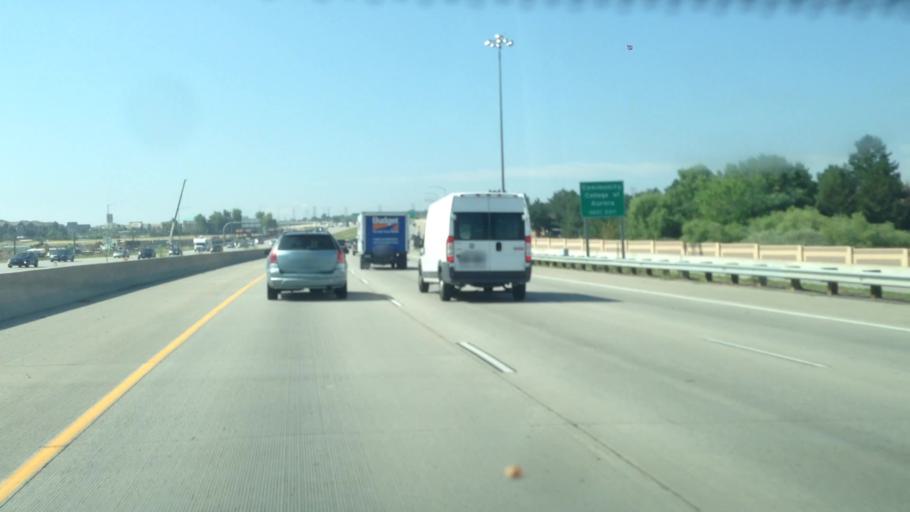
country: US
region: Colorado
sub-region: Adams County
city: Aurora
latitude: 39.7251
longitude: -104.8250
